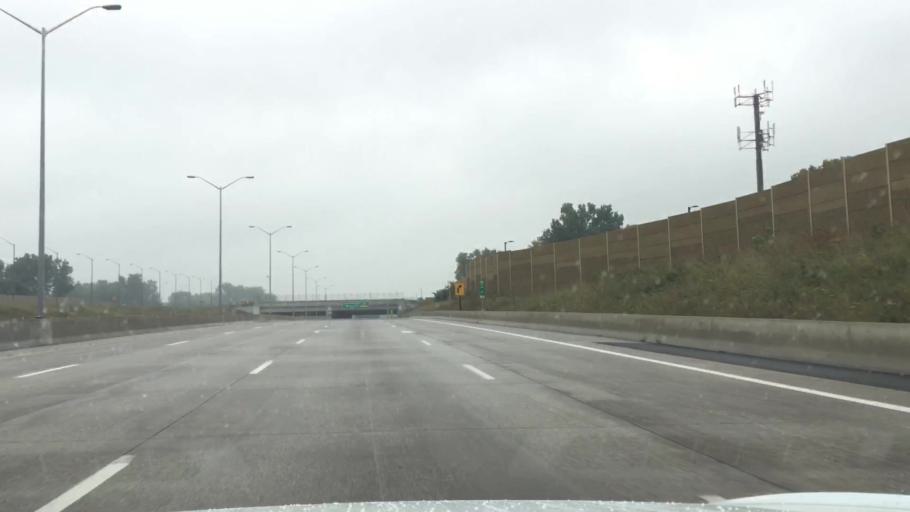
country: CA
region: Ontario
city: Windsor
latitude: 42.2609
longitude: -83.0418
